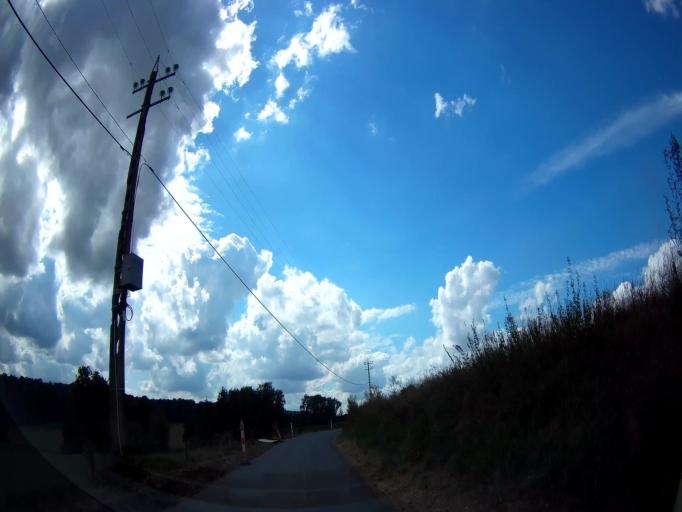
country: BE
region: Wallonia
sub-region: Province de Namur
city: Havelange
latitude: 50.4225
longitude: 5.2099
